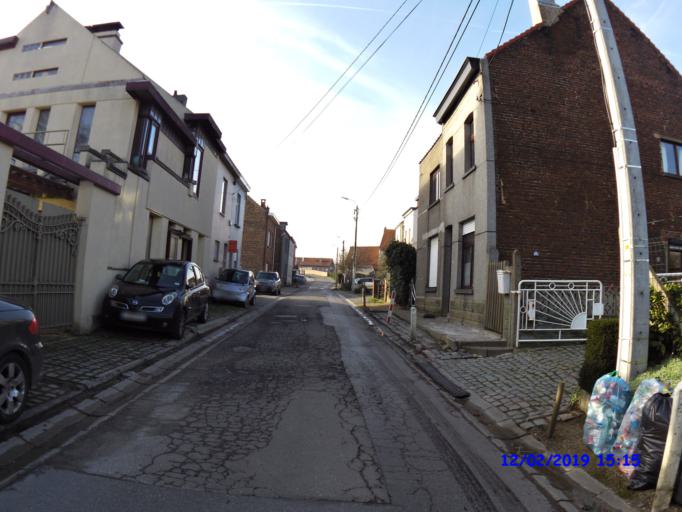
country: BE
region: Flanders
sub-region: Provincie Vlaams-Brabant
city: Sint-Genesius-Rode
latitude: 50.7638
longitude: 4.3590
